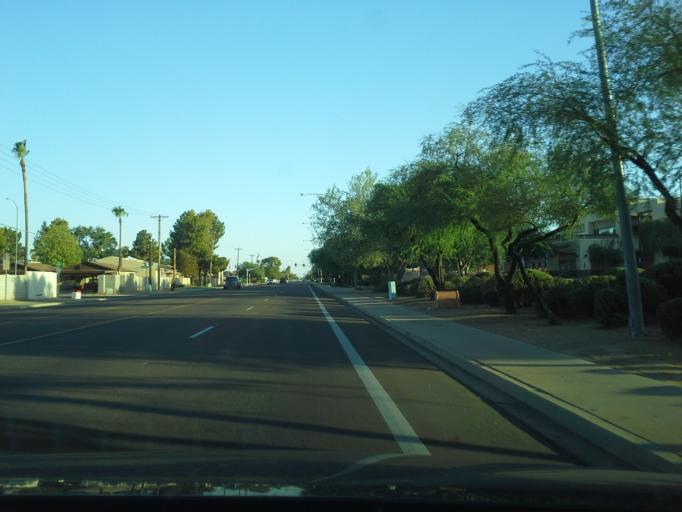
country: US
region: Arizona
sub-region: Maricopa County
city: Mesa
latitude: 33.4282
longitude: -111.8229
